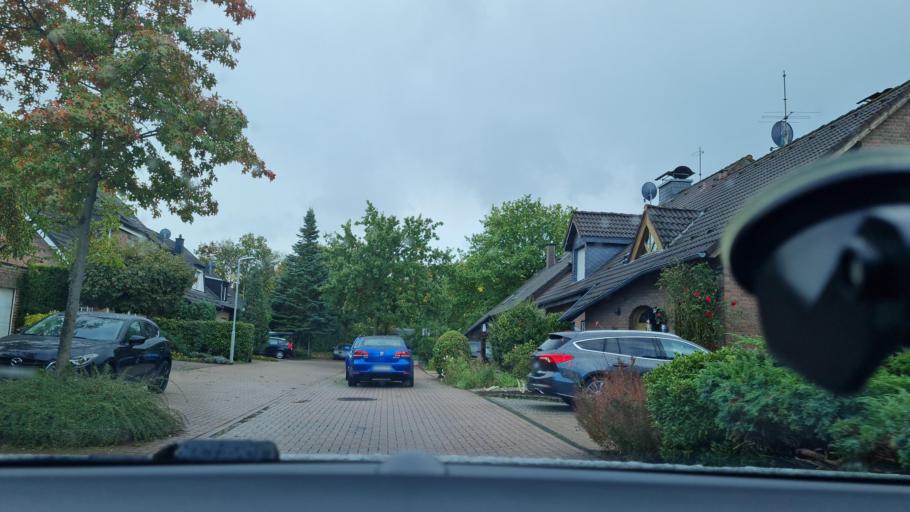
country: DE
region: North Rhine-Westphalia
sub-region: Regierungsbezirk Dusseldorf
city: Dinslaken
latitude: 51.5521
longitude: 6.7444
